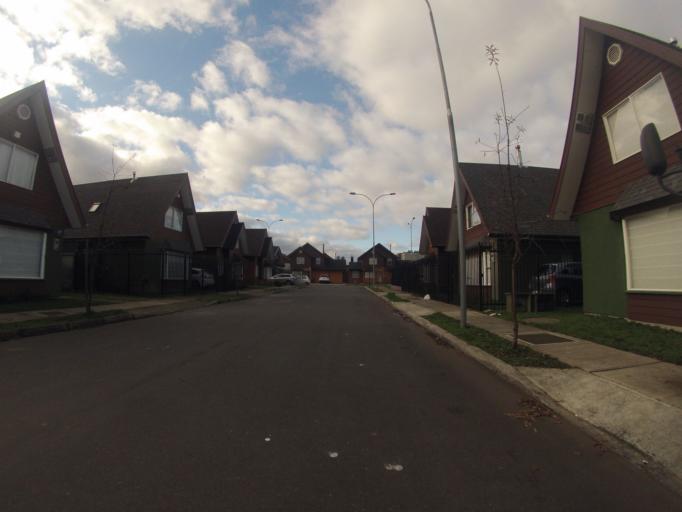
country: CL
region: Araucania
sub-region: Provincia de Cautin
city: Temuco
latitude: -38.7422
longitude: -72.6456
